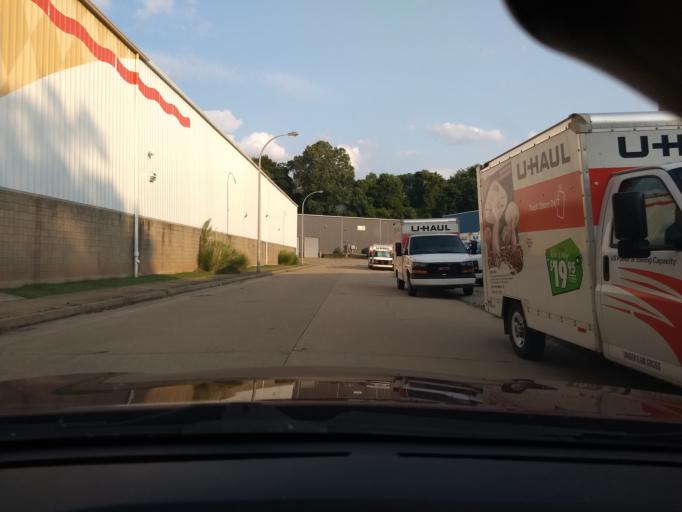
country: US
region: Pennsylvania
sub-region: Allegheny County
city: Aspinwall
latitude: 40.4620
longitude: -79.9043
